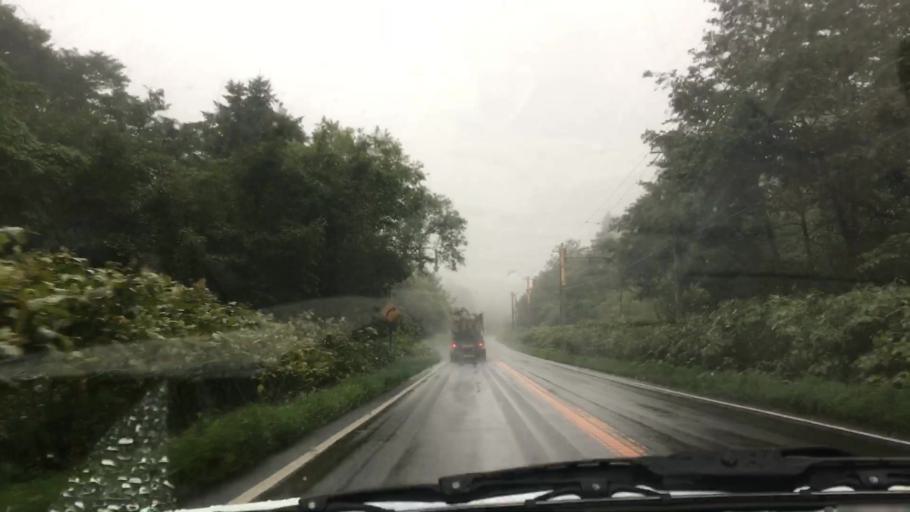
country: JP
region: Hokkaido
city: Niseko Town
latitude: 42.5927
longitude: 140.5182
